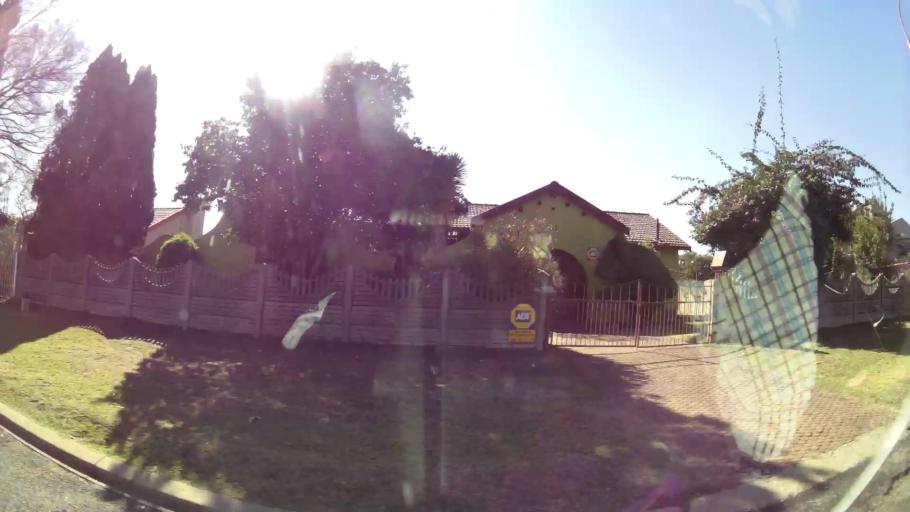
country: ZA
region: Gauteng
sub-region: Ekurhuleni Metropolitan Municipality
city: Tembisa
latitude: -26.0362
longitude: 28.2322
